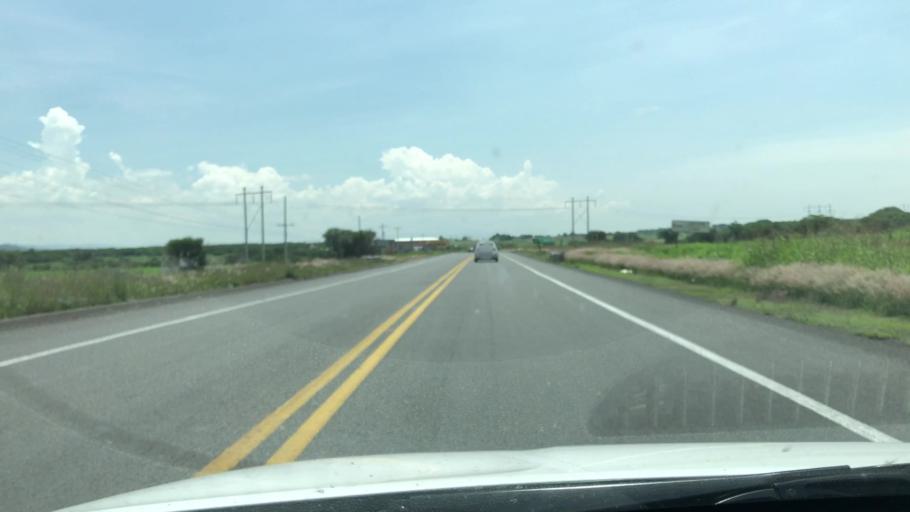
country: MX
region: Jalisco
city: Degollado
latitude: 20.3615
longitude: -102.1471
